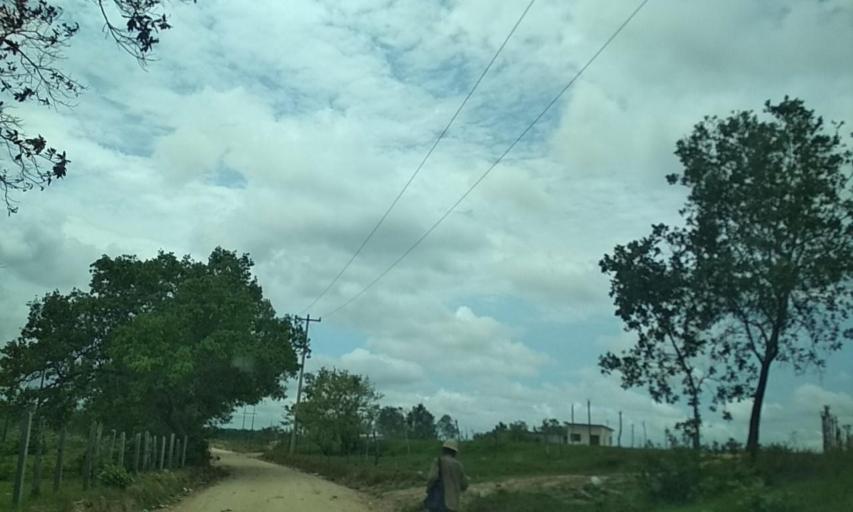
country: MX
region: Veracruz
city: Las Choapas
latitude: 17.8989
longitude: -94.1202
